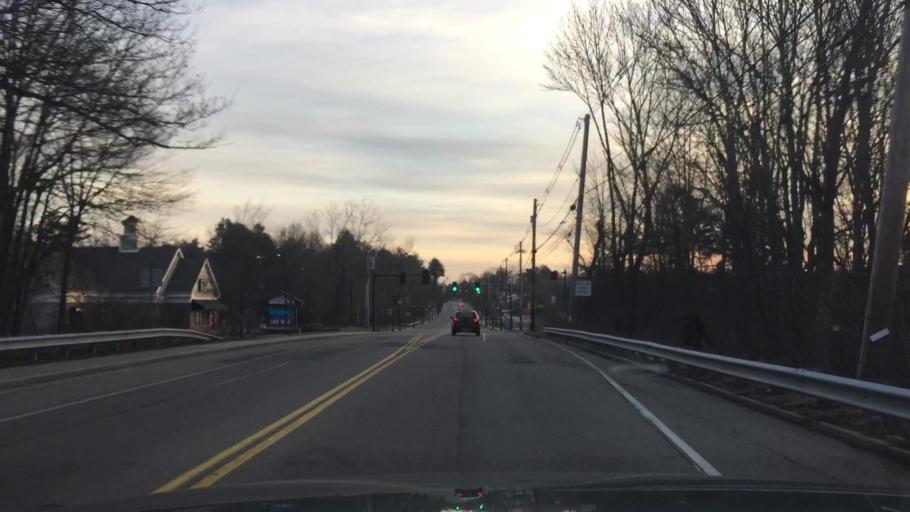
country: US
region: Massachusetts
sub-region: Norfolk County
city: Millis
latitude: 42.1622
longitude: -71.3717
